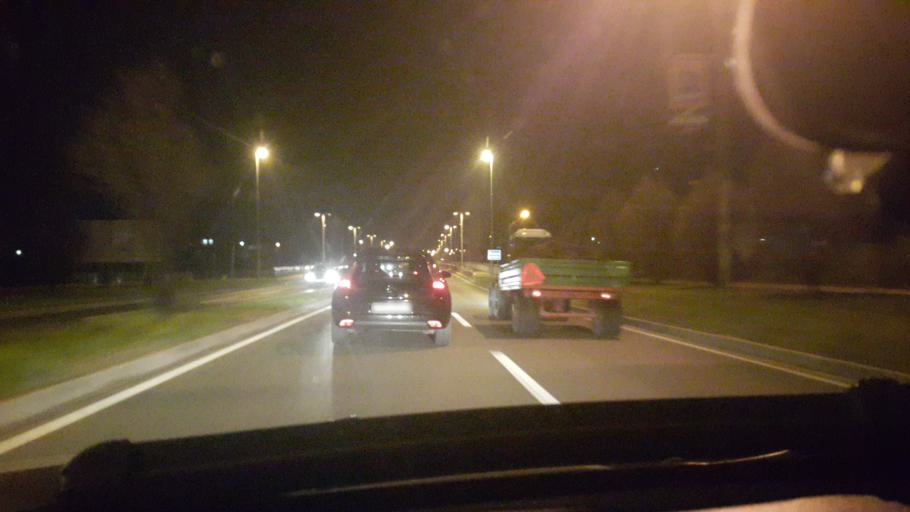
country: SI
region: Maribor
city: Kamnica
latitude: 46.5620
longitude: 15.6274
